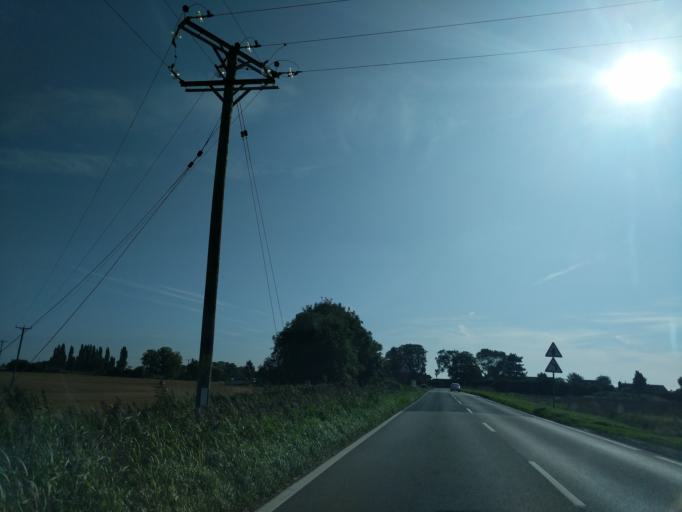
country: GB
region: England
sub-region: Lincolnshire
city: Langtoft
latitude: 52.7720
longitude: -0.2943
